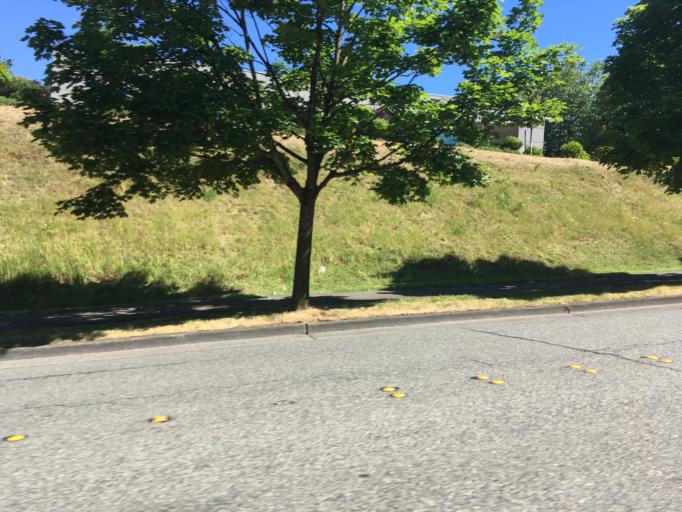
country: US
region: Washington
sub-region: King County
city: Redmond
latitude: 47.6315
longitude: -122.1460
